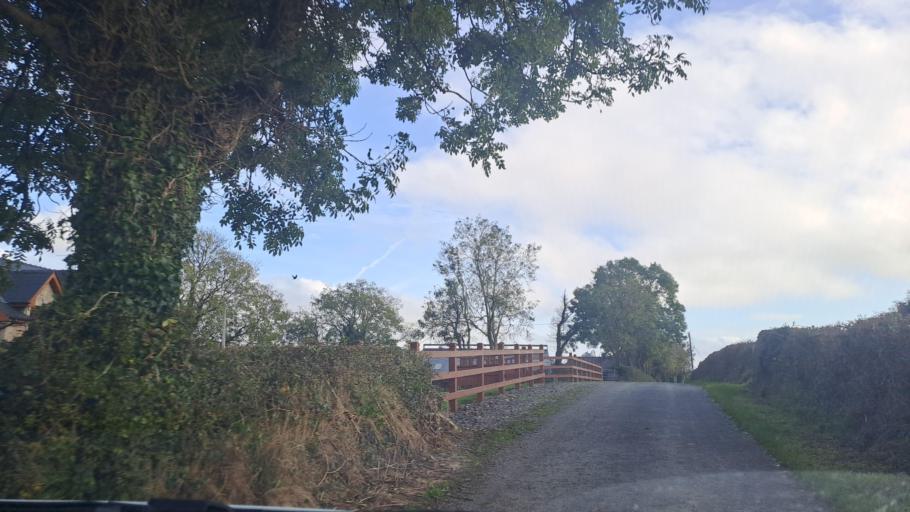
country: IE
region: Ulster
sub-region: County Monaghan
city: Carrickmacross
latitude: 54.0108
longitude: -6.7497
